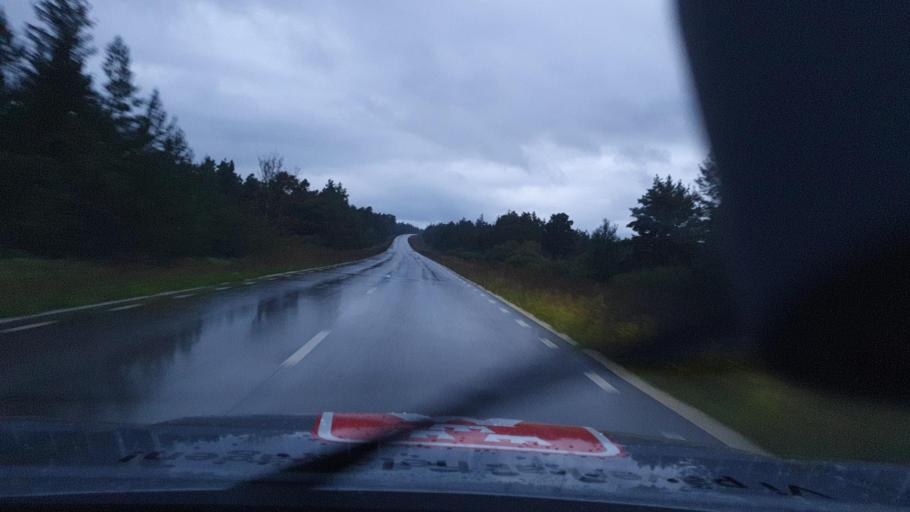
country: SE
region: Gotland
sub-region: Gotland
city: Slite
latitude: 57.7387
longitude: 18.7906
